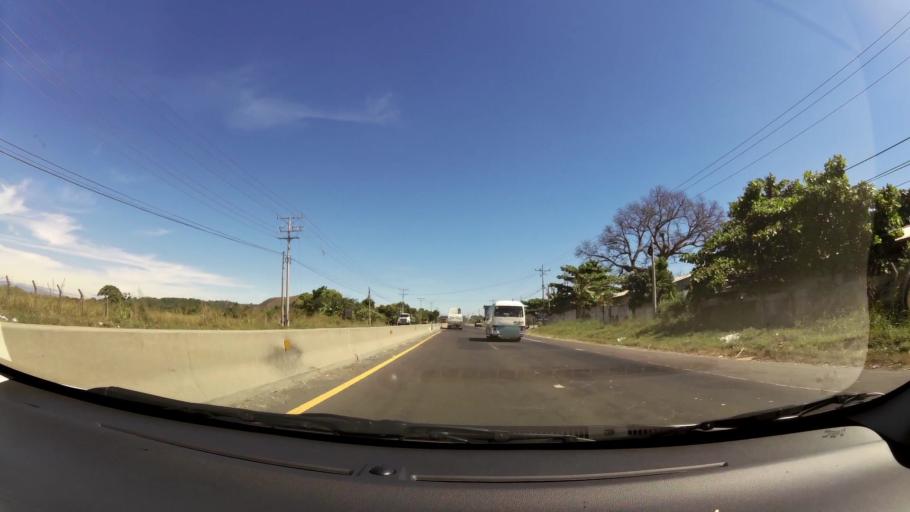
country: SV
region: La Libertad
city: San Juan Opico
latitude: 13.7929
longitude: -89.3498
